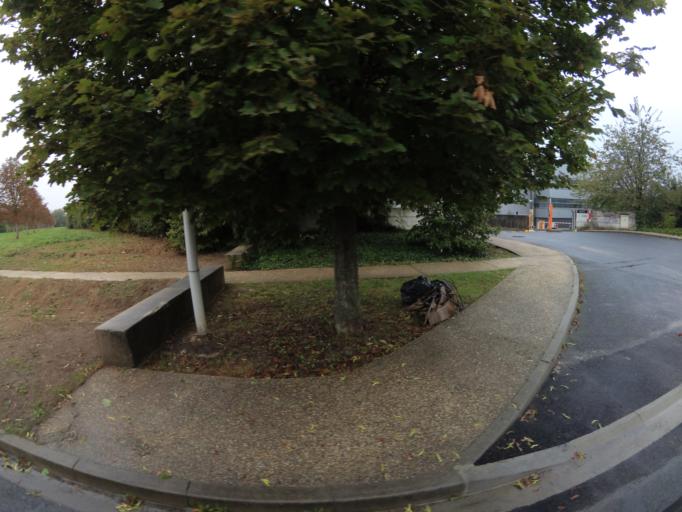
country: FR
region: Ile-de-France
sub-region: Departement de Seine-et-Marne
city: Ferrieres-en-Brie
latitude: 48.8316
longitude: 2.7234
